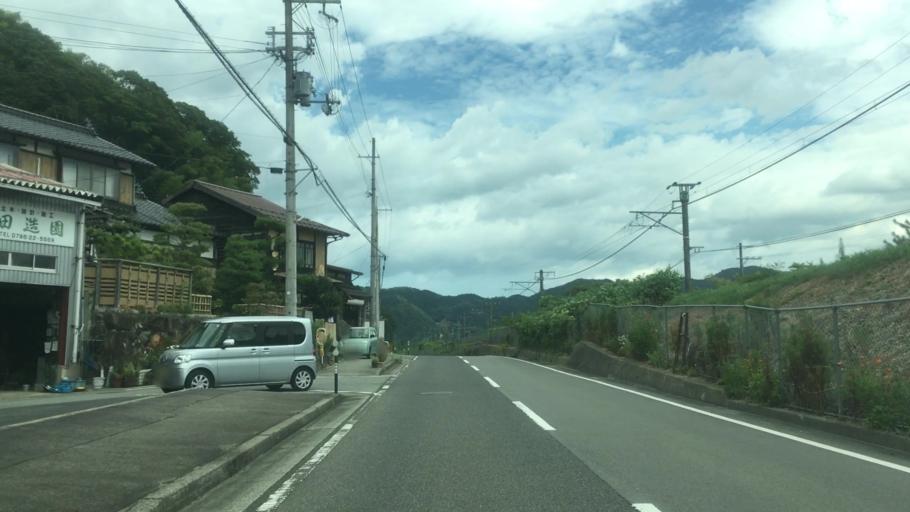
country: JP
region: Hyogo
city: Toyooka
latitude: 35.5668
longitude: 134.8036
